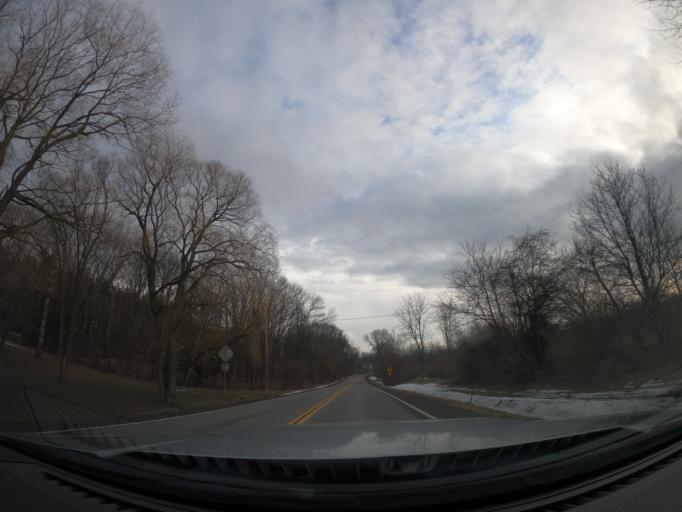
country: US
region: New York
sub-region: Yates County
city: Dundee
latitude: 42.5129
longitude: -76.9650
